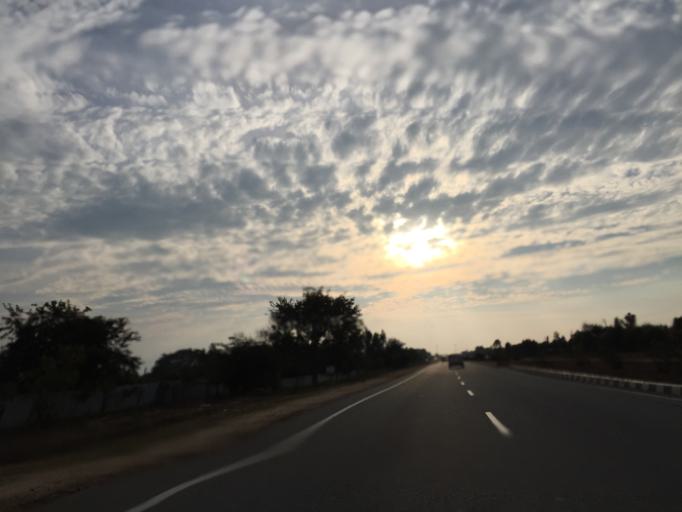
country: IN
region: Karnataka
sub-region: Kolar
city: Kolar
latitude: 13.1446
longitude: 78.2408
